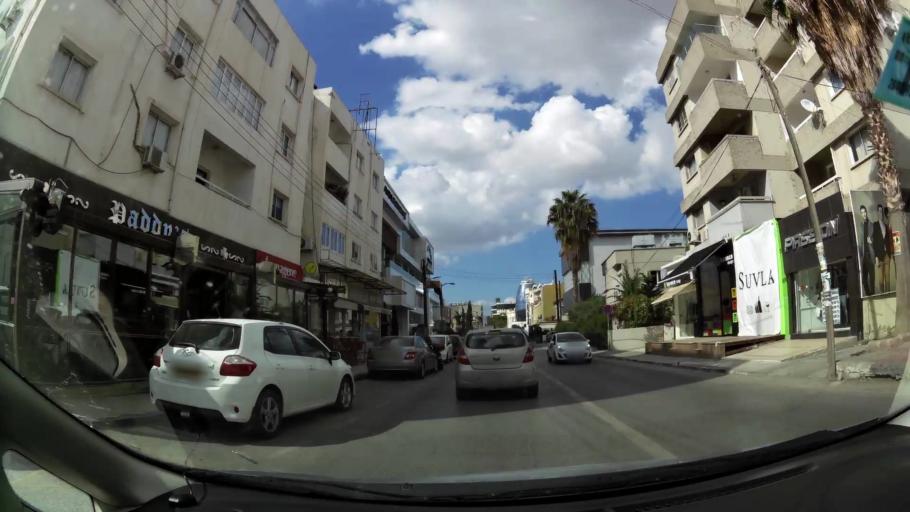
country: CY
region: Lefkosia
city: Nicosia
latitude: 35.1883
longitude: 33.3501
